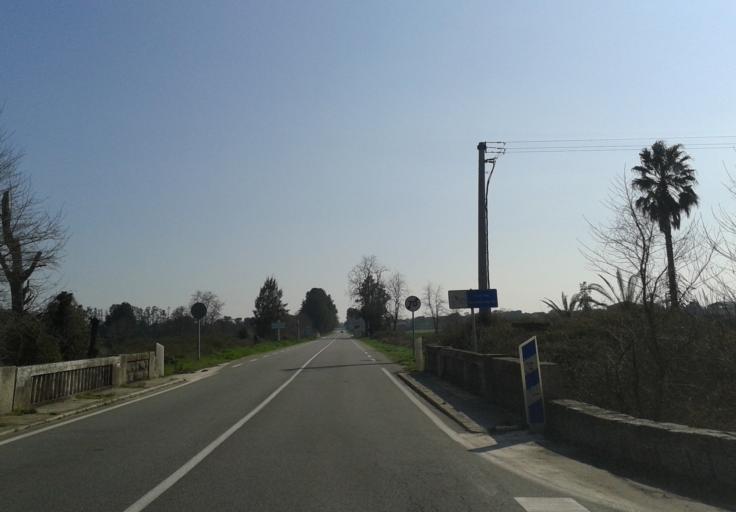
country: FR
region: Corsica
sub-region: Departement de la Haute-Corse
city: Linguizzetta
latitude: 42.2504
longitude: 9.5455
